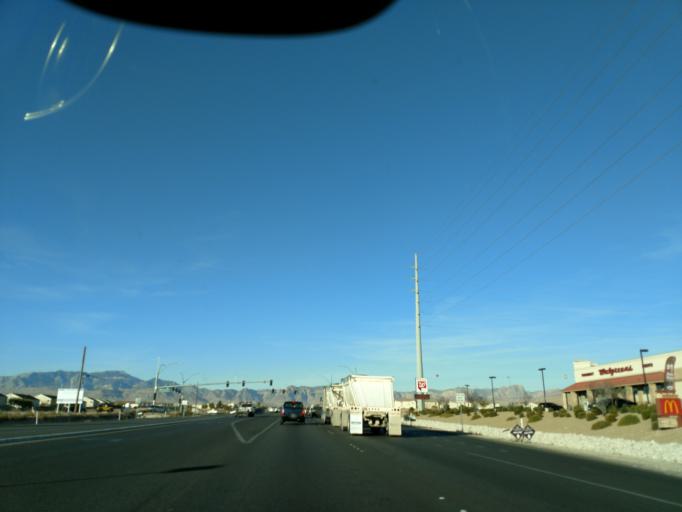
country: US
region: Nevada
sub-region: Clark County
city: Enterprise
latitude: 36.0204
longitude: -115.2776
